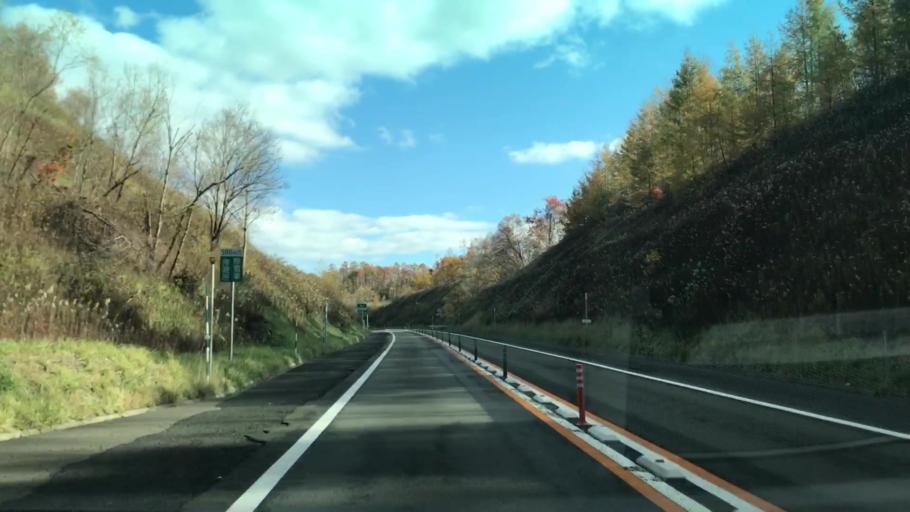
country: JP
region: Hokkaido
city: Chitose
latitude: 42.9131
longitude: 141.9261
